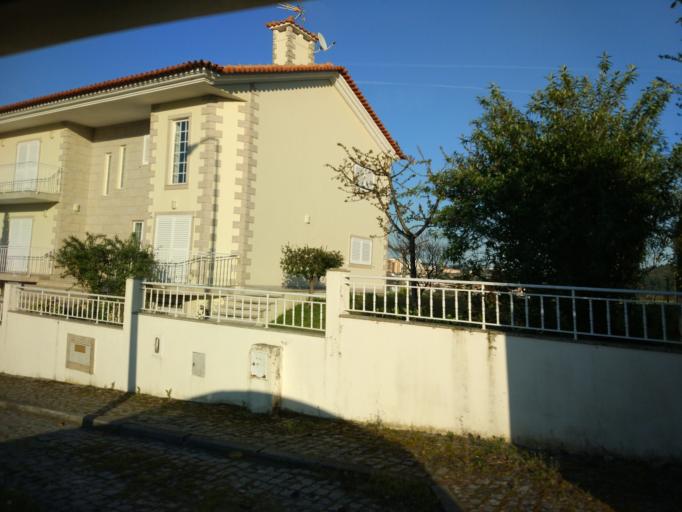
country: PT
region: Vila Real
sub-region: Vila Real
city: Vila Real
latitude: 41.2985
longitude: -7.7651
